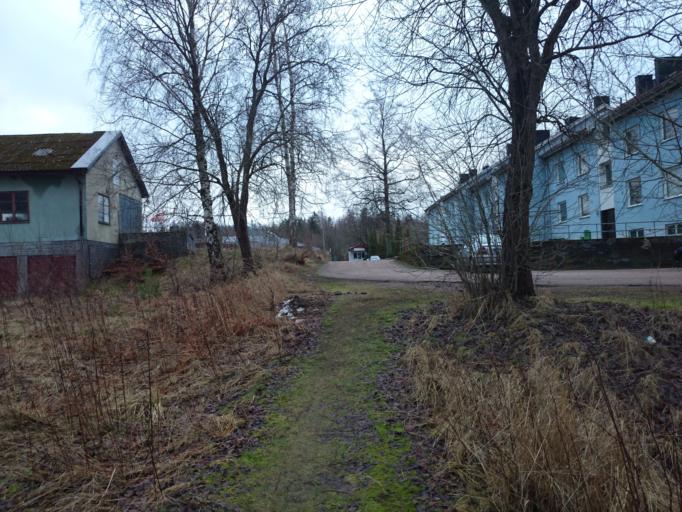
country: SE
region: Halland
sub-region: Hylte Kommun
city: Hyltebruk
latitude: 57.0020
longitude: 13.2515
